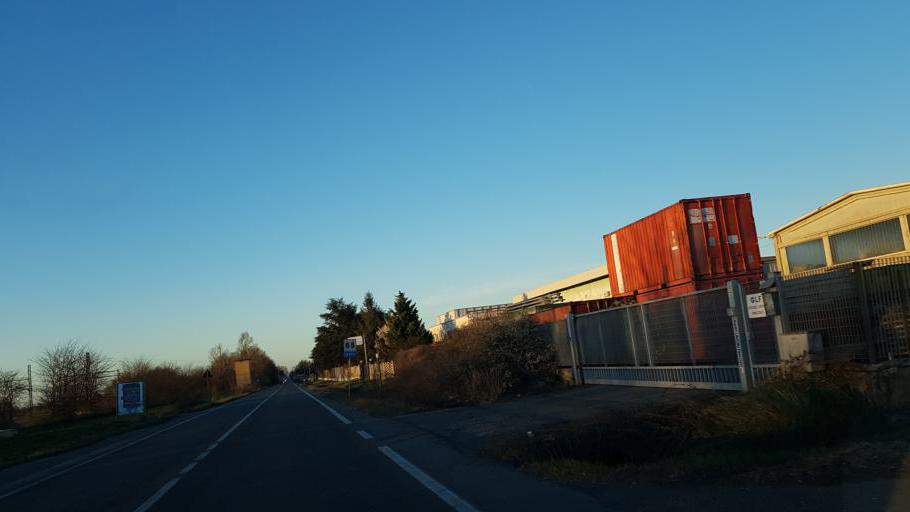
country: IT
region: Piedmont
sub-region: Provincia di Alessandria
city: Carbonara Scrivia
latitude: 44.8511
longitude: 8.8539
